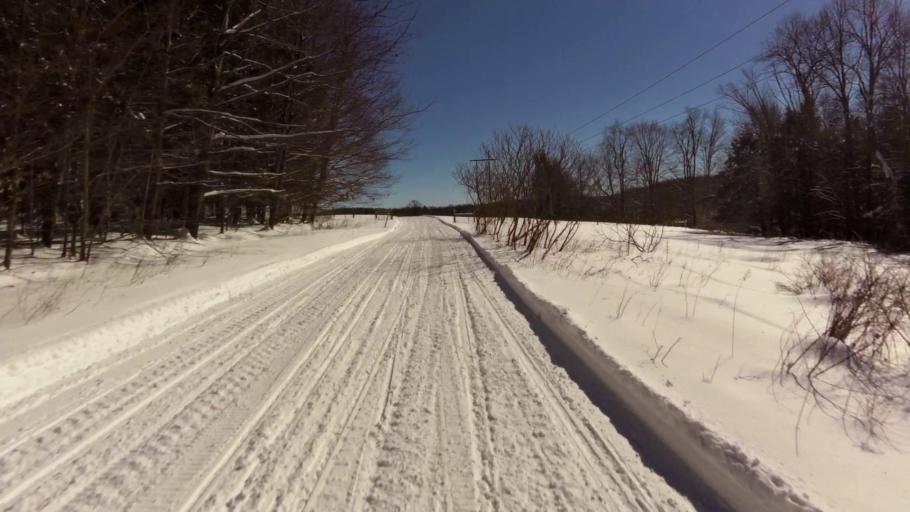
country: US
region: New York
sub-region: Chautauqua County
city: Mayville
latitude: 42.2282
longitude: -79.5209
